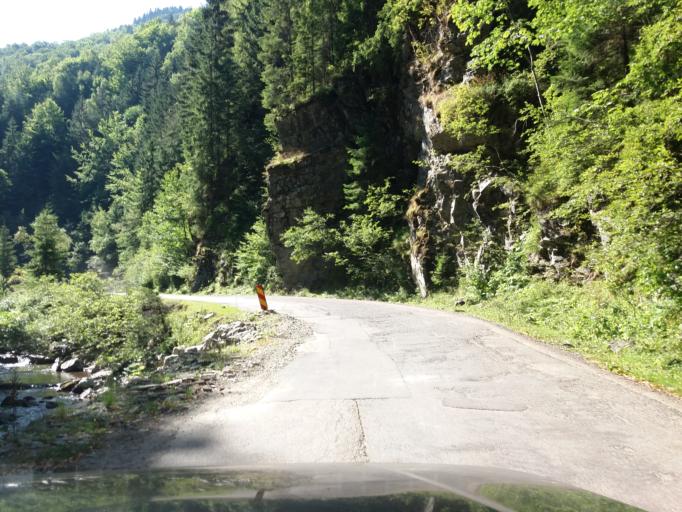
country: RO
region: Hunedoara
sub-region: Oras Petrila
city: Petrila
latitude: 45.4117
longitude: 23.4743
